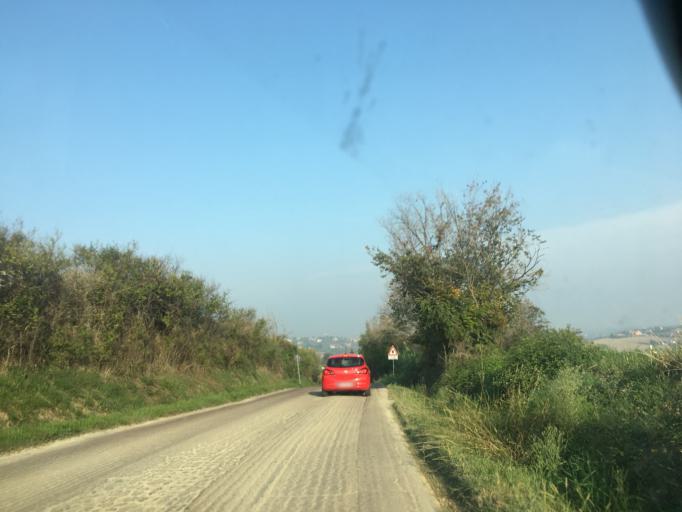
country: IT
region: Emilia-Romagna
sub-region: Provincia di Rimini
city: San Clemente
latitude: 43.9446
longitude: 12.6207
